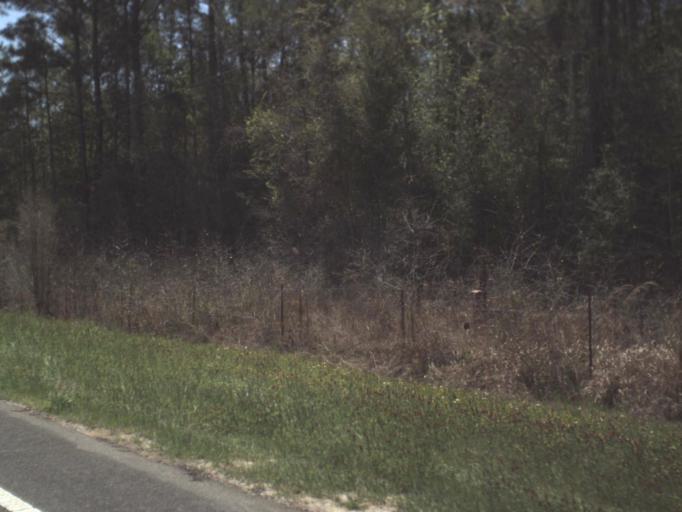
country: US
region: Florida
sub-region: Walton County
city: DeFuniak Springs
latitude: 30.8329
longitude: -85.9537
